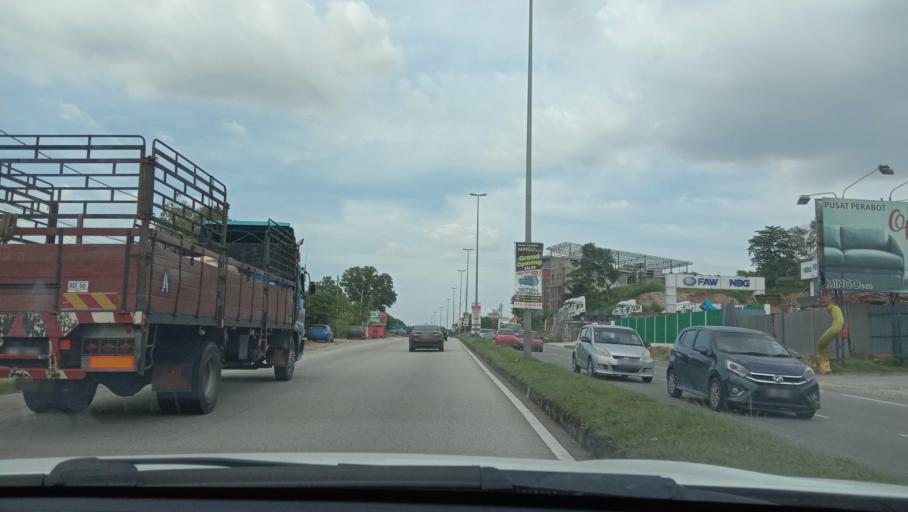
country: MY
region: Selangor
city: Kampung Baru Subang
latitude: 3.1336
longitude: 101.5259
